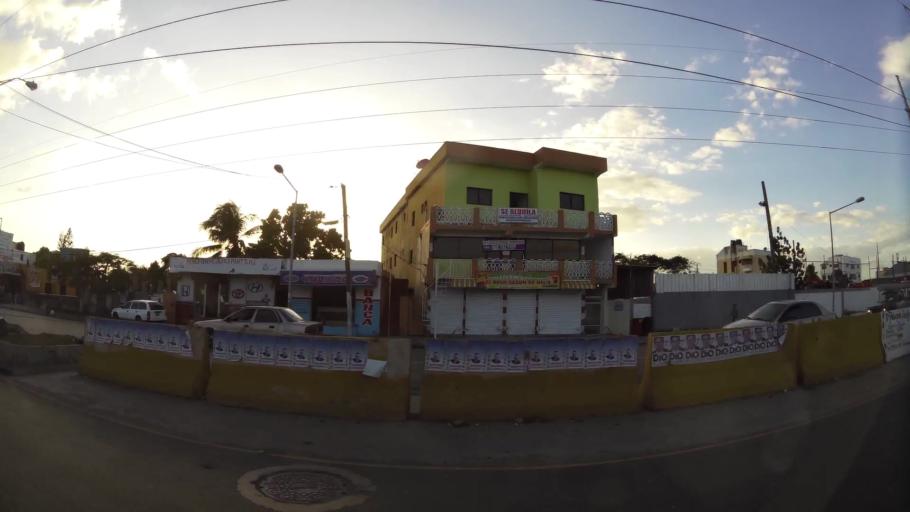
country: DO
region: Santo Domingo
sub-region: Santo Domingo
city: Santo Domingo Este
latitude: 18.4865
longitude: -69.8262
